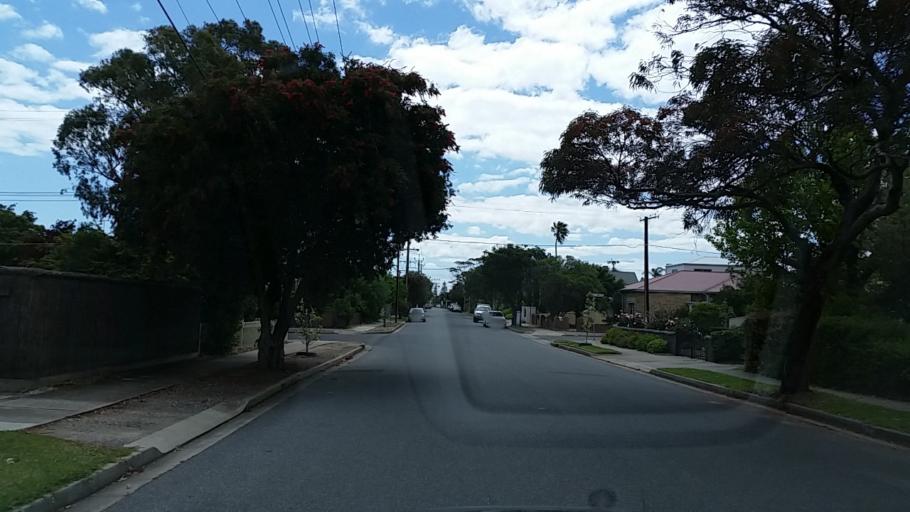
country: AU
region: South Australia
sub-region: Holdfast Bay
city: North Brighton
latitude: -34.9937
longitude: 138.5161
